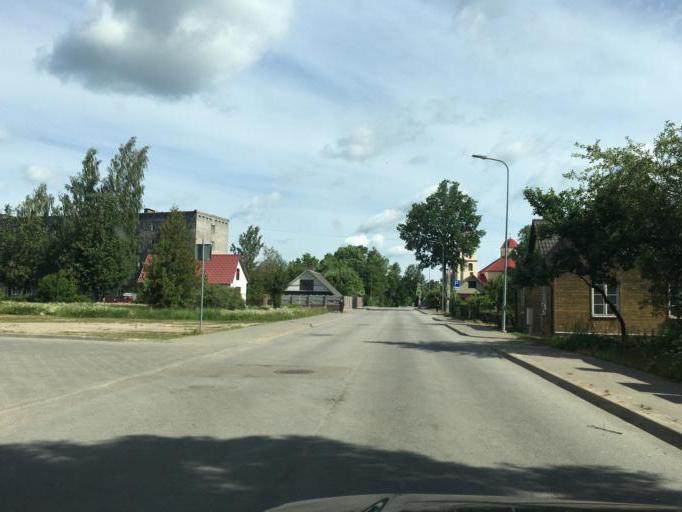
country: LV
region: Balvu Rajons
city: Balvi
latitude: 57.1322
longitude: 27.2710
